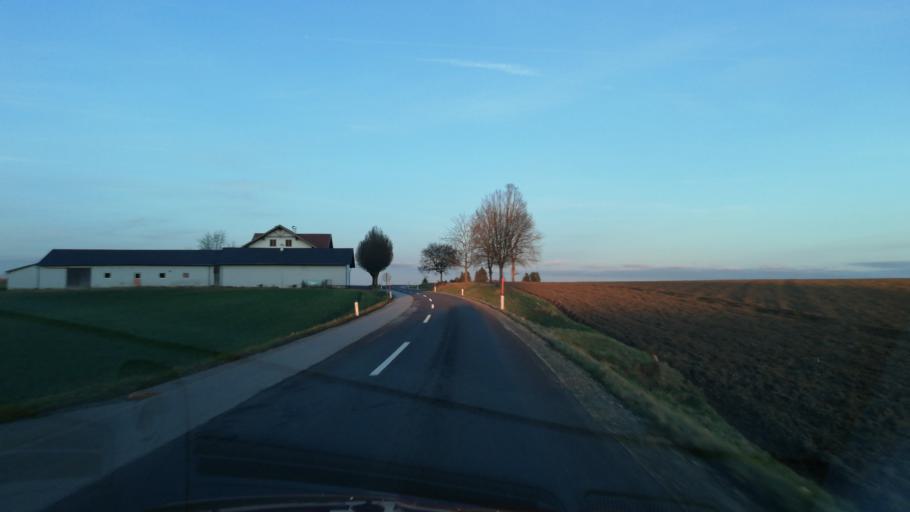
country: DE
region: Bavaria
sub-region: Lower Bavaria
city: Ering
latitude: 48.2233
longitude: 13.1269
